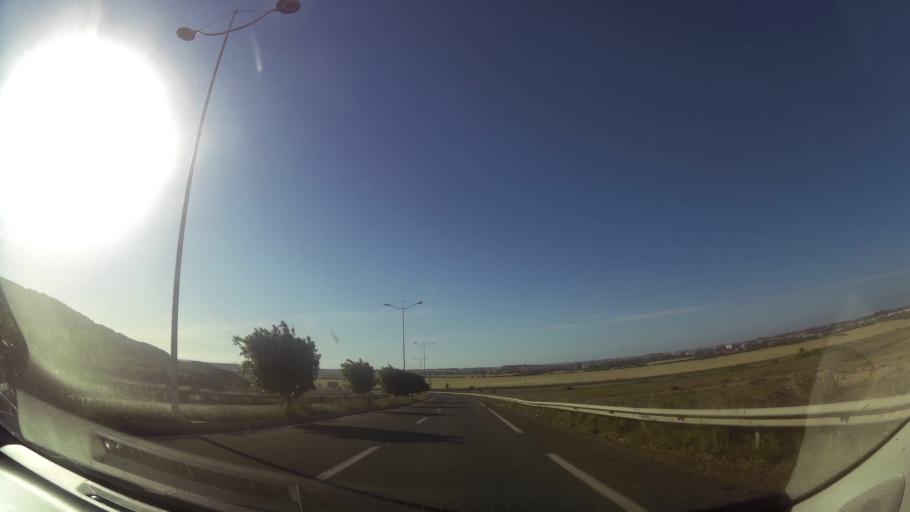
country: MA
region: Oriental
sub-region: Berkane-Taourirt
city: Madagh
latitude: 35.0620
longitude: -2.2241
